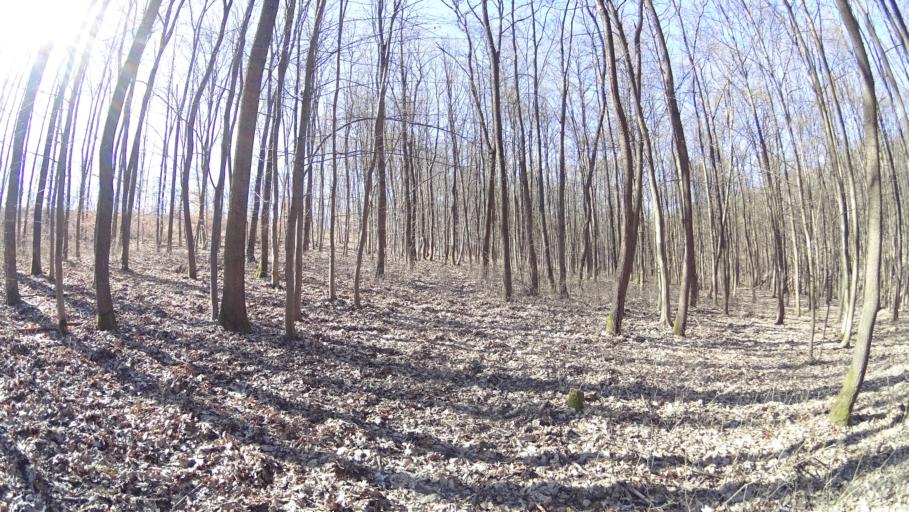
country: HU
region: Pest
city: Veroce
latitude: 47.8650
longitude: 19.0817
